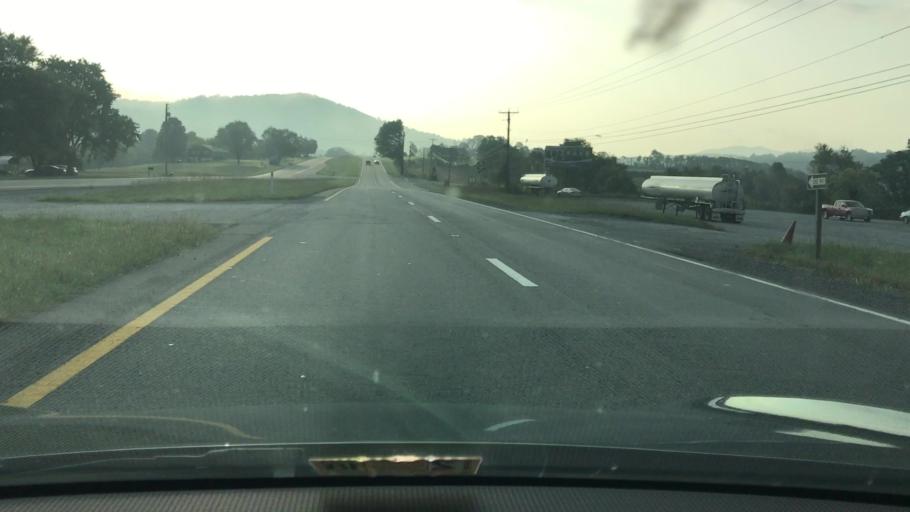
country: US
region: Virginia
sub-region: Botetourt County
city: Blue Ridge
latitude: 37.3785
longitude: -79.7157
